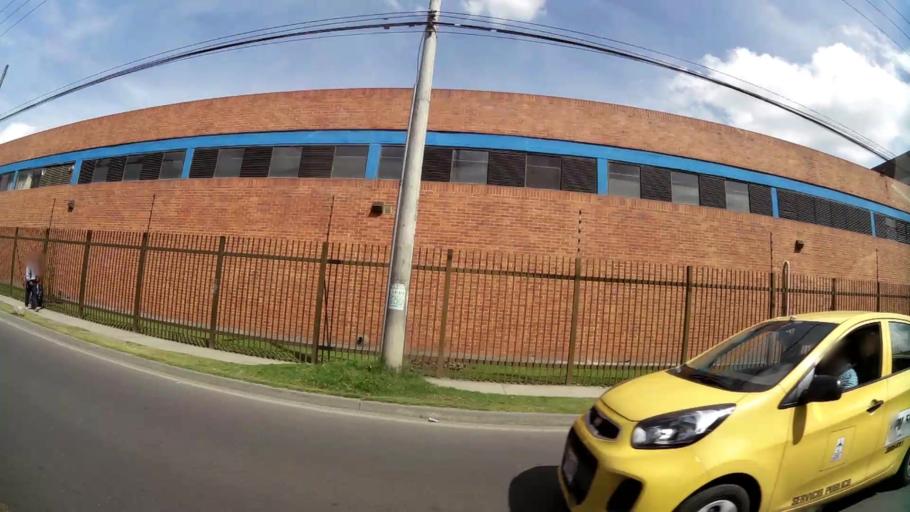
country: CO
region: Bogota D.C.
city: Bogota
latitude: 4.6487
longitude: -74.1367
